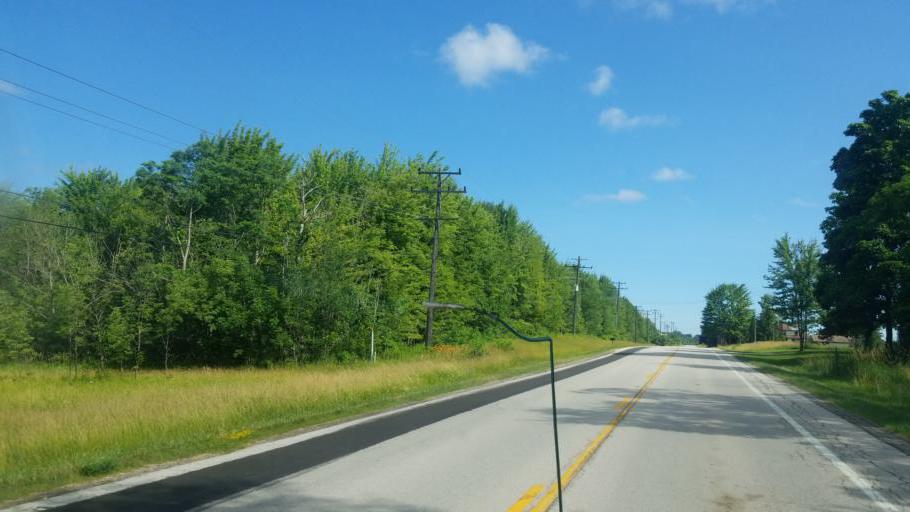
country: US
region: Ohio
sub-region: Ashtabula County
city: Conneaut
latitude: 41.8771
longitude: -80.5722
